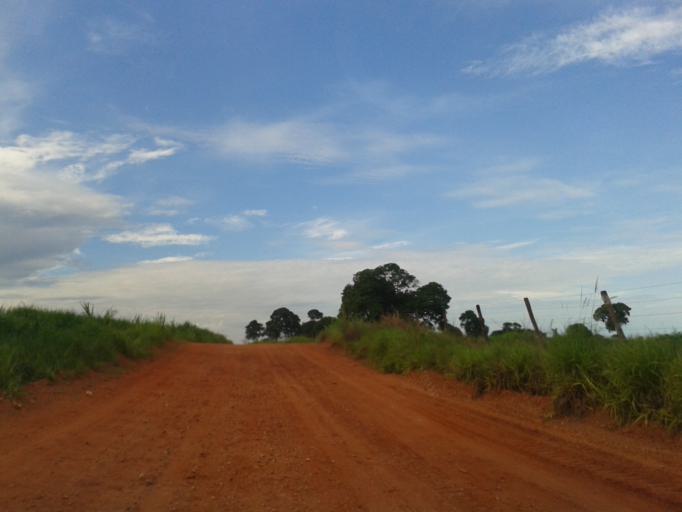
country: BR
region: Minas Gerais
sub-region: Santa Vitoria
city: Santa Vitoria
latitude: -19.0764
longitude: -50.4813
